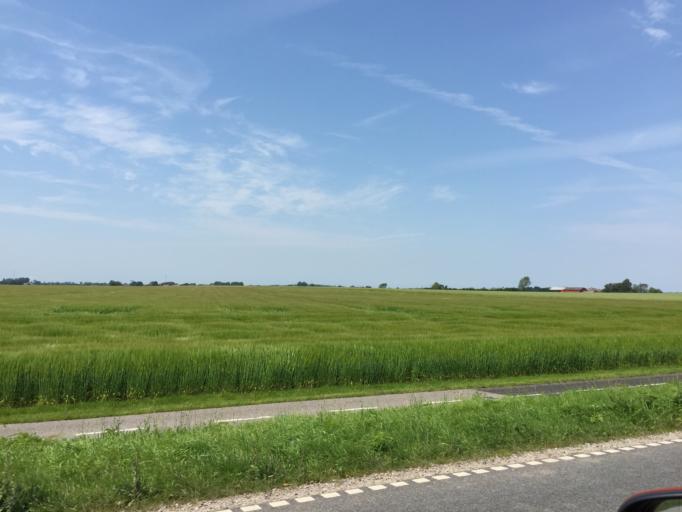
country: DK
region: South Denmark
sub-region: Kerteminde Kommune
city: Kerteminde
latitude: 55.4274
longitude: 10.6520
